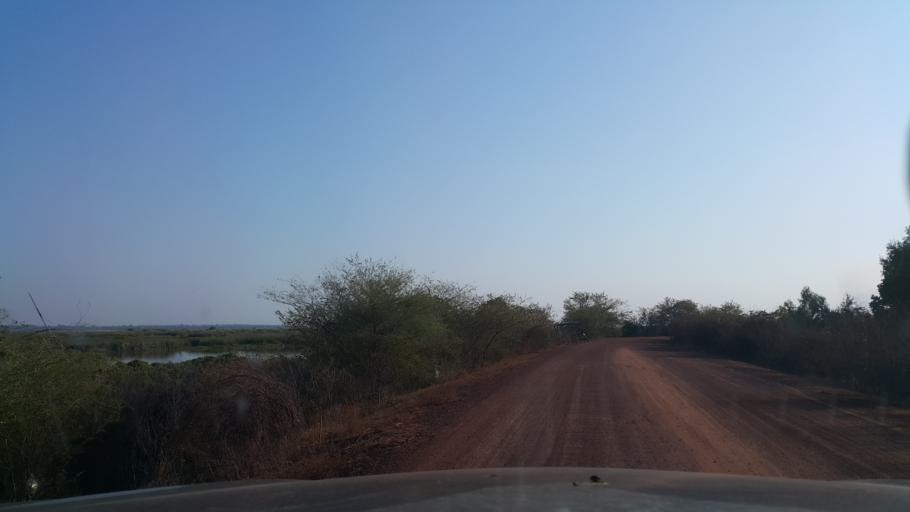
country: TH
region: Changwat Udon Thani
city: Ban Na Muang
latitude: 17.2257
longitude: 103.0491
